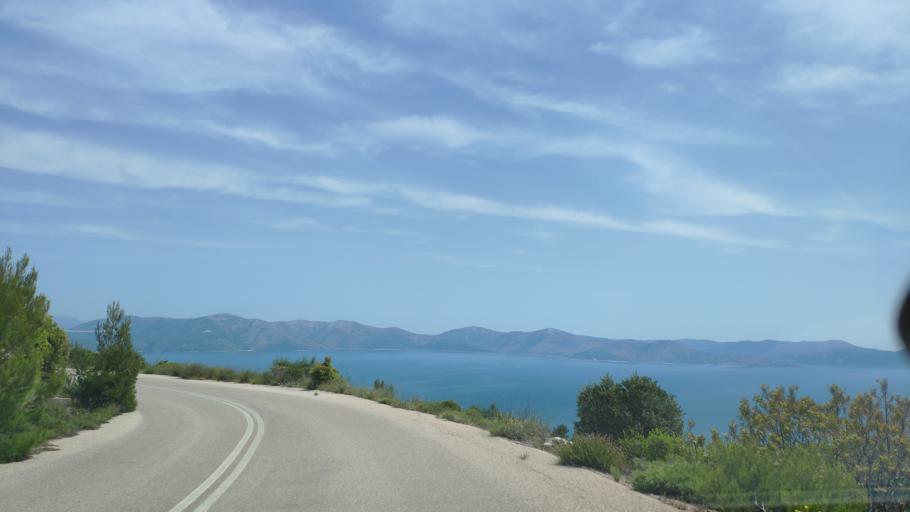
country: GR
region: Attica
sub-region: Nomarchia Anatolikis Attikis
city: Grammatiko
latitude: 38.2473
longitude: 23.9655
